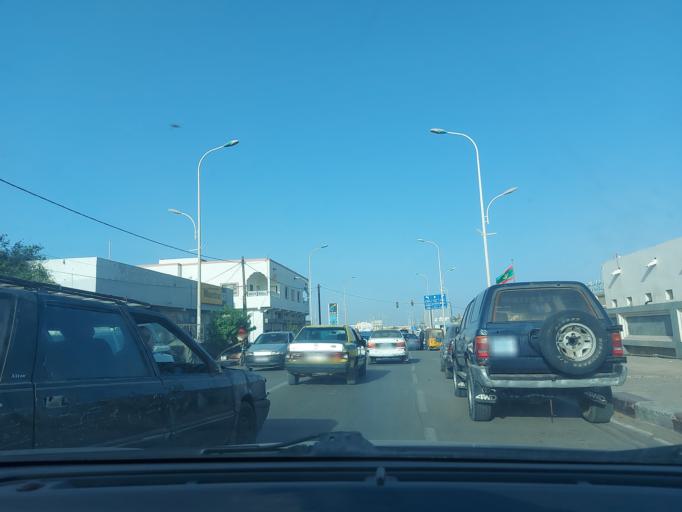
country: MR
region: Nouakchott
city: Nouakchott
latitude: 18.0856
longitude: -15.9901
